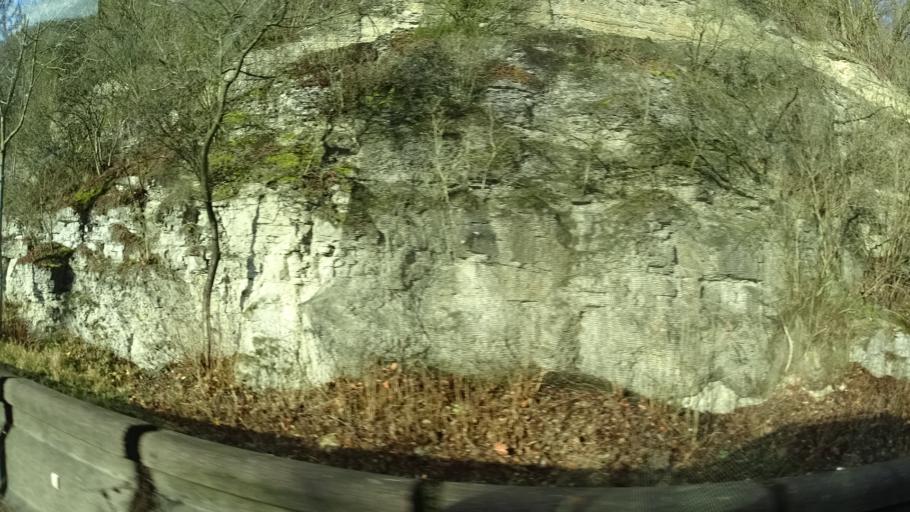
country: DE
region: Thuringia
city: Arnstadt
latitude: 50.8234
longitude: 10.9478
